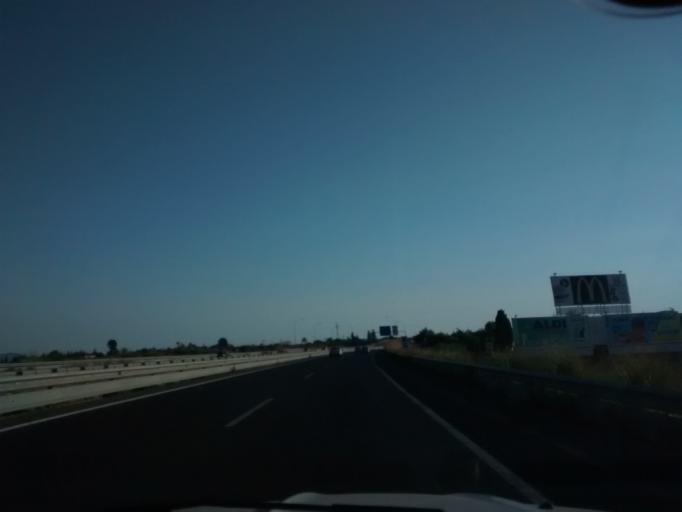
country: ES
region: Balearic Islands
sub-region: Illes Balears
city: Inca
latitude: 39.7192
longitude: 2.9271
